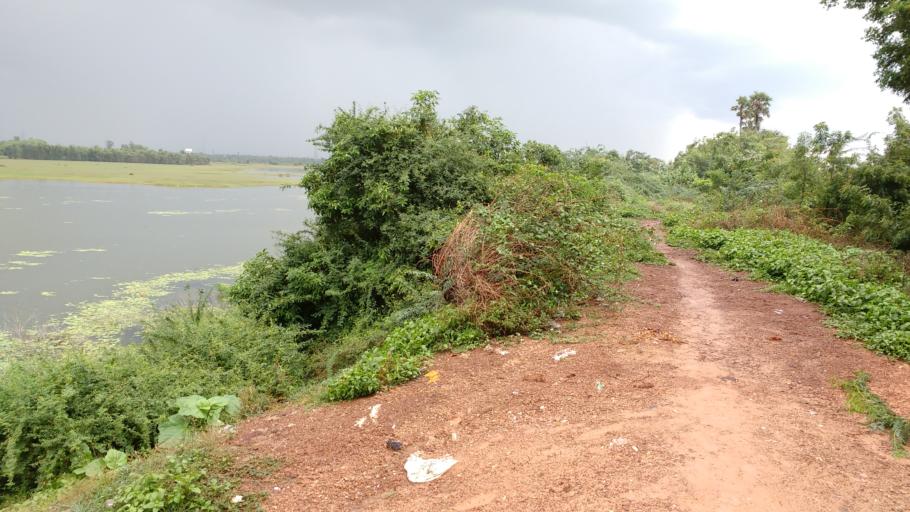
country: IN
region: Tamil Nadu
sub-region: Kancheepuram
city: Sriperumbudur
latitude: 12.9707
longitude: 79.9406
